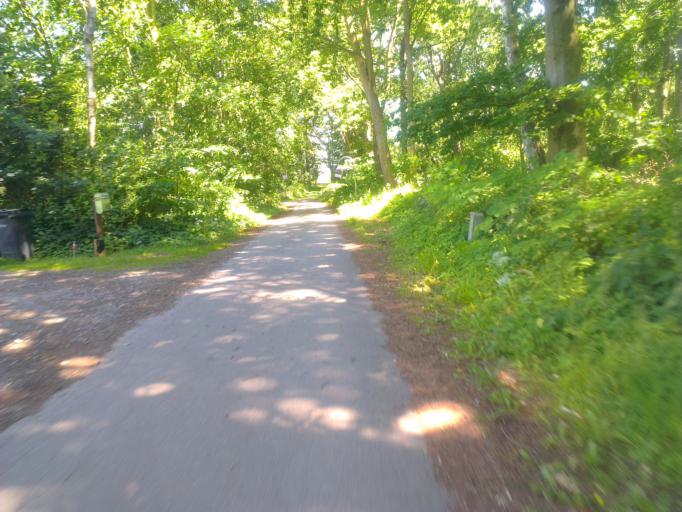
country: DK
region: Capital Region
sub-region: Frederikssund Kommune
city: Jaegerspris
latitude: 55.9271
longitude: 11.9595
